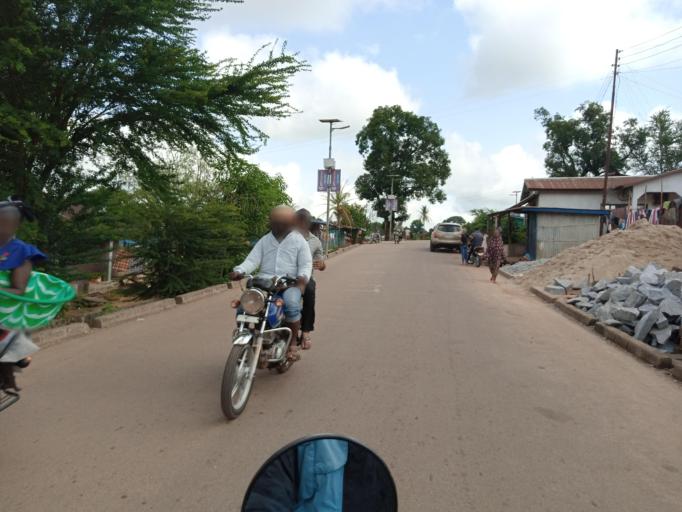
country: SL
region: Southern Province
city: Bo
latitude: 7.9738
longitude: -11.7385
